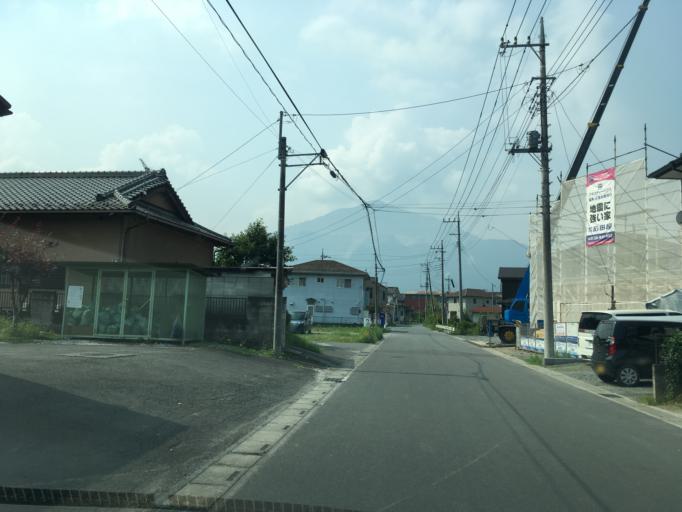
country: JP
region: Saitama
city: Chichibu
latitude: 35.9984
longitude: 139.1062
